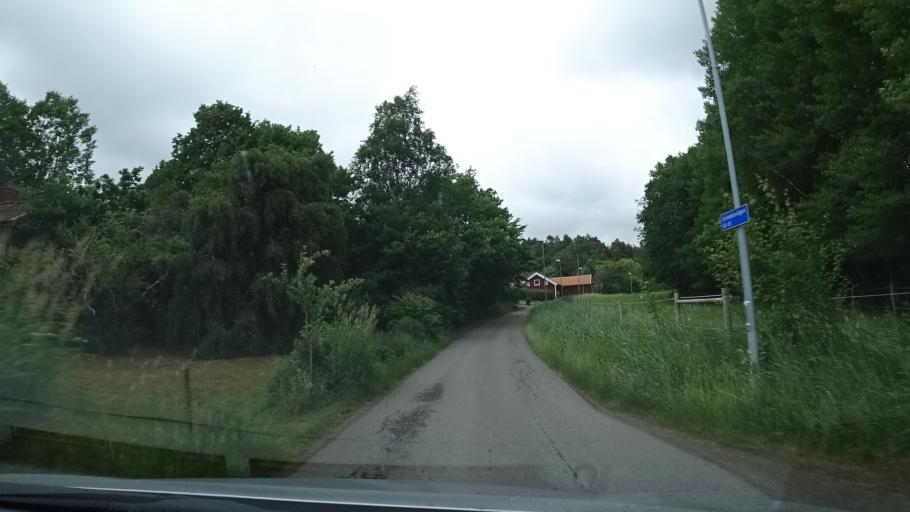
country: SE
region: Vaestra Goetaland
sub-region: Goteborg
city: Billdal
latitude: 57.5854
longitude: 11.9559
